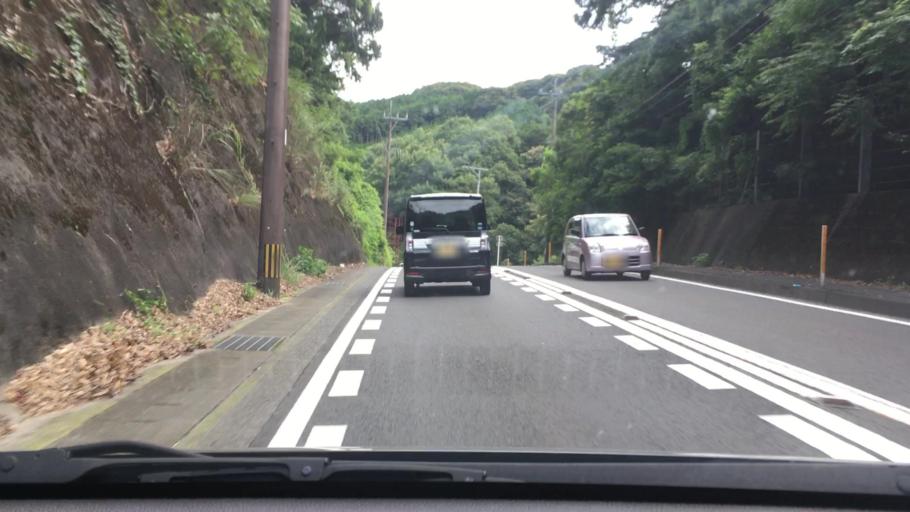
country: JP
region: Nagasaki
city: Togitsu
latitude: 32.9299
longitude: 129.7825
